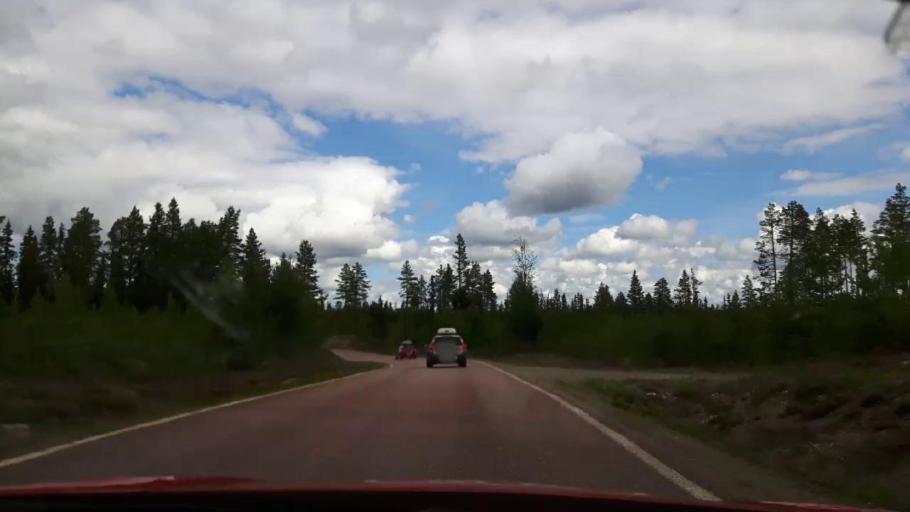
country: NO
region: Hedmark
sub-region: Trysil
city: Innbygda
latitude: 61.8696
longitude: 12.9592
